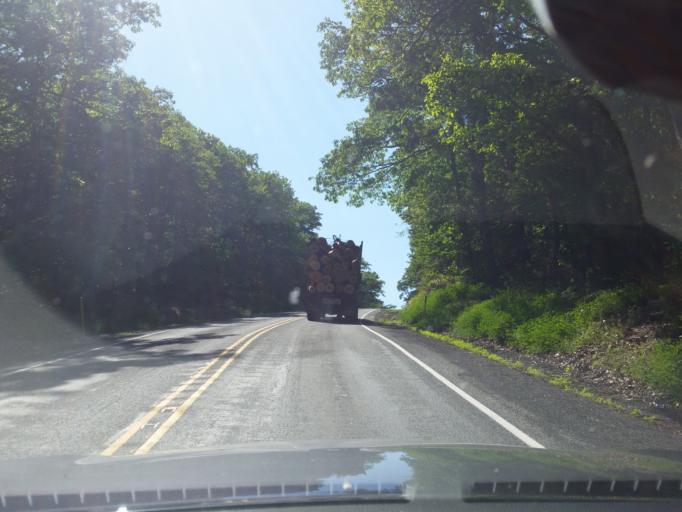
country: US
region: Pennsylvania
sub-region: Lycoming County
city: Duboistown
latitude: 41.1378
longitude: -77.0831
